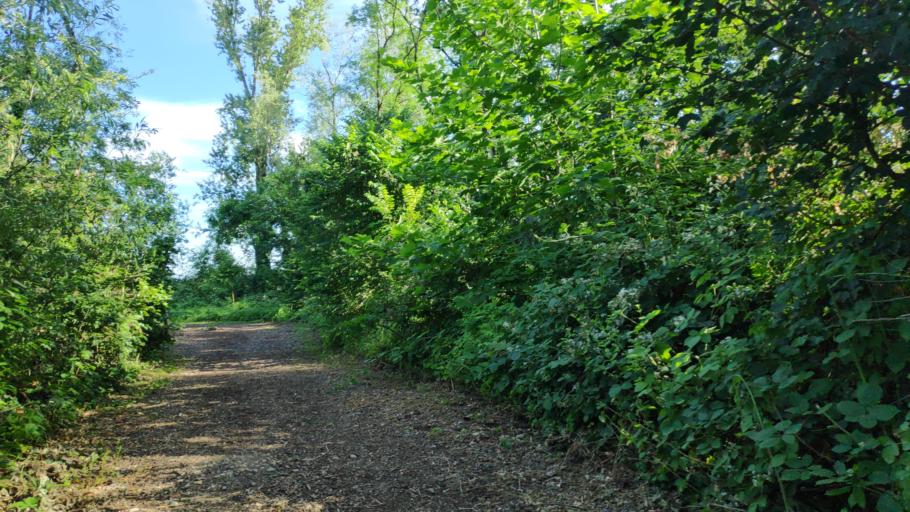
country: IT
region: Lombardy
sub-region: Citta metropolitana di Milano
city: Basiglio
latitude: 45.3508
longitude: 9.1485
